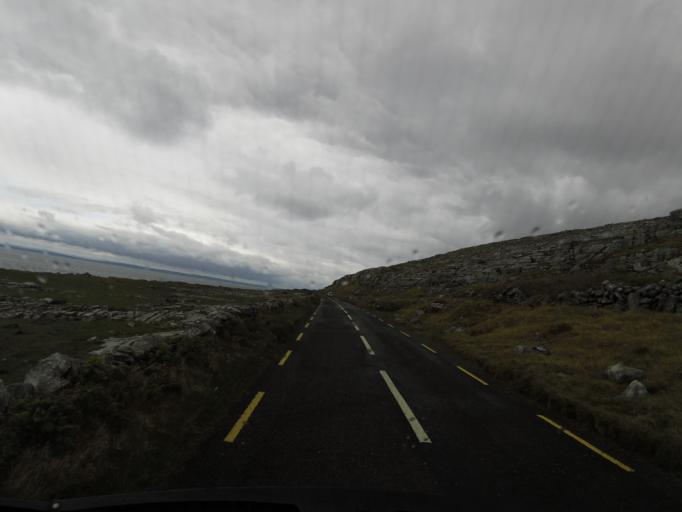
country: IE
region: Connaught
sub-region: County Galway
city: Bearna
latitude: 53.1493
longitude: -9.2698
